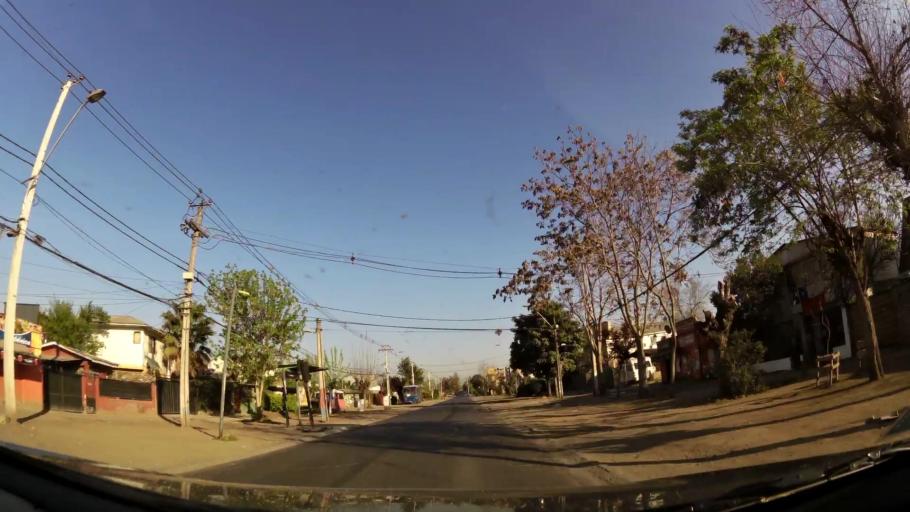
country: CL
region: Santiago Metropolitan
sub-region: Provincia de Santiago
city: Santiago
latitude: -33.3949
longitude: -70.6300
